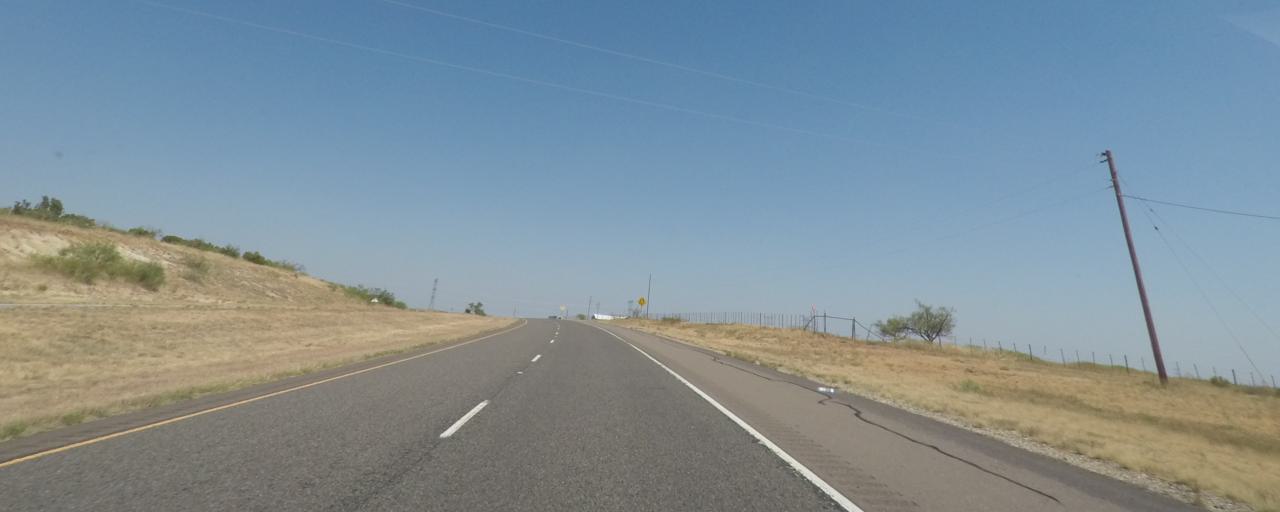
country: US
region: Texas
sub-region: Dickens County
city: Dickens
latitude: 33.6202
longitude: -100.8578
